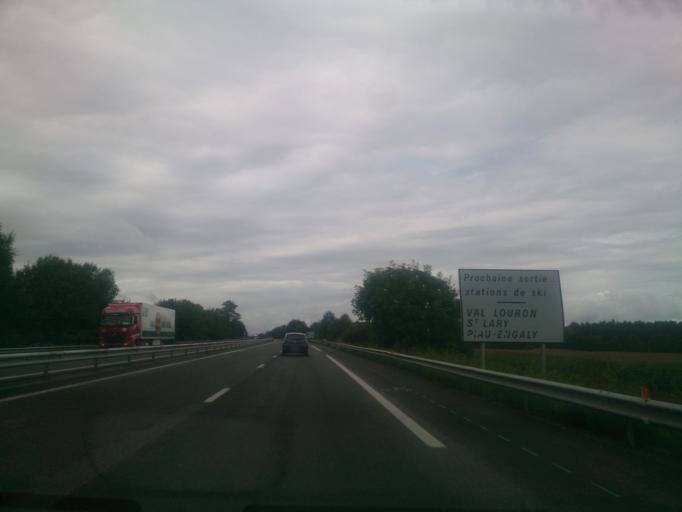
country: FR
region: Midi-Pyrenees
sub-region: Departement des Hautes-Pyrenees
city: La Barthe-de-Neste
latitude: 43.1034
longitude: 0.4213
